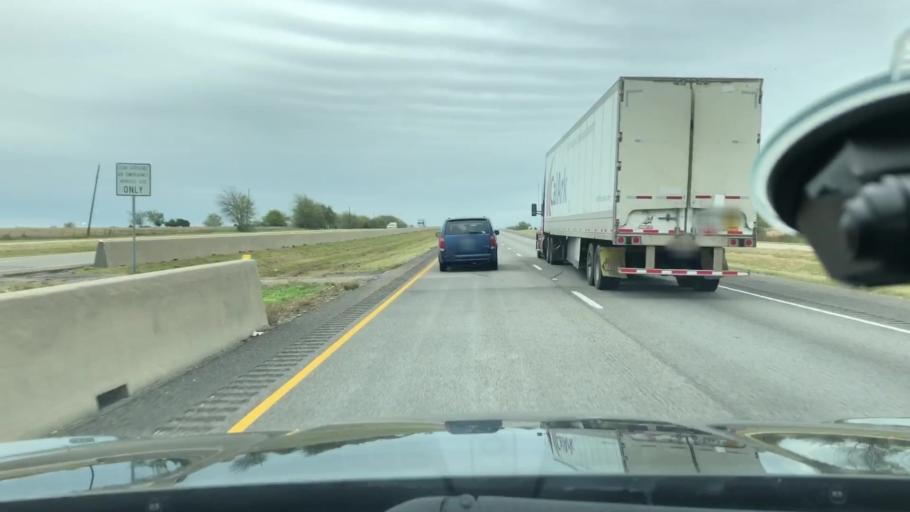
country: US
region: Texas
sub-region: Hunt County
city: Commerce
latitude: 33.1294
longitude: -95.8594
